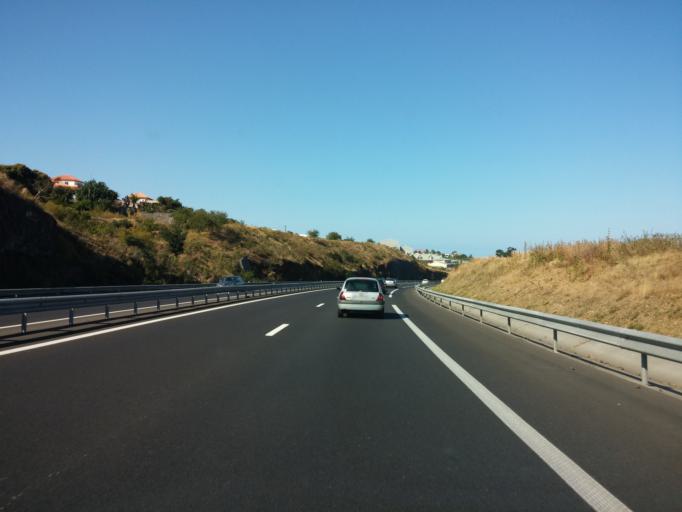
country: RE
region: Reunion
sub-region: Reunion
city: Saint-Leu
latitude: -21.1948
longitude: 55.2961
